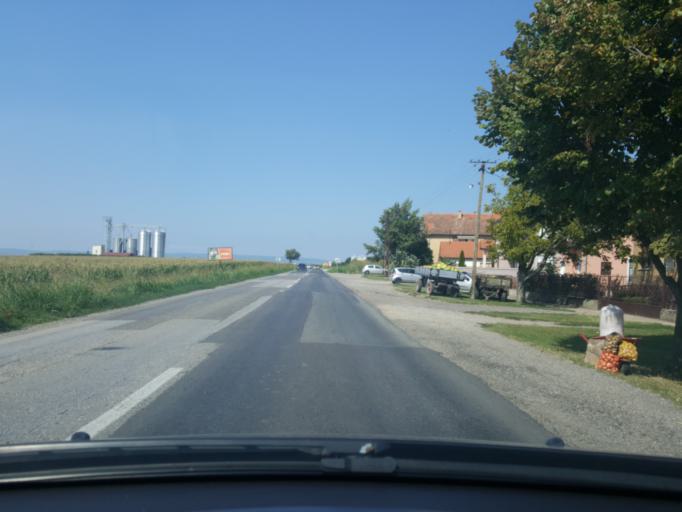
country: RS
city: Jarak
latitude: 44.9182
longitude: 19.7700
